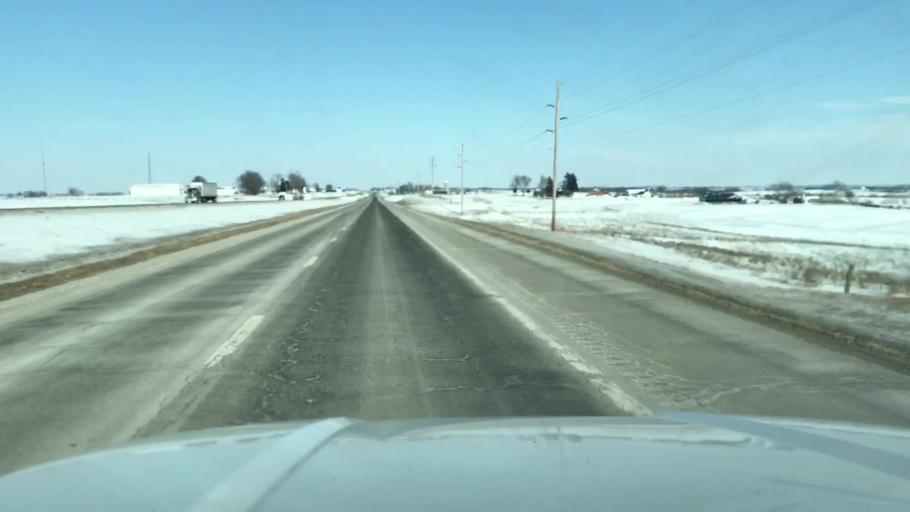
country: US
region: Missouri
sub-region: Nodaway County
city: Maryville
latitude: 40.2331
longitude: -94.8675
